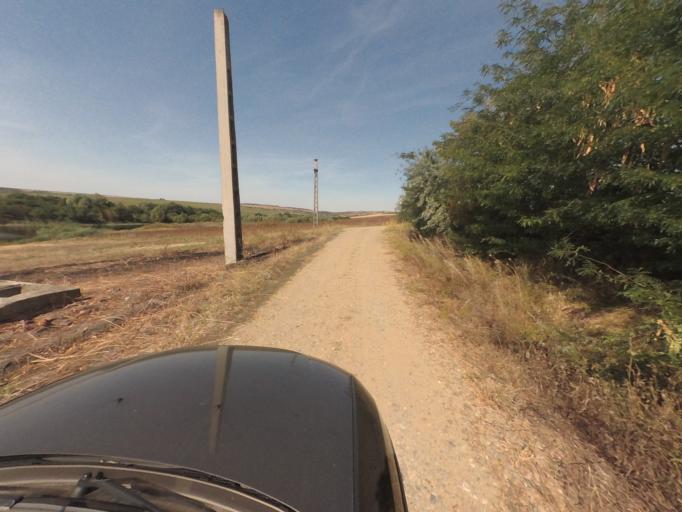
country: RO
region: Vaslui
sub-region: Comuna Costesti
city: Costesti
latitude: 46.5248
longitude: 27.7386
